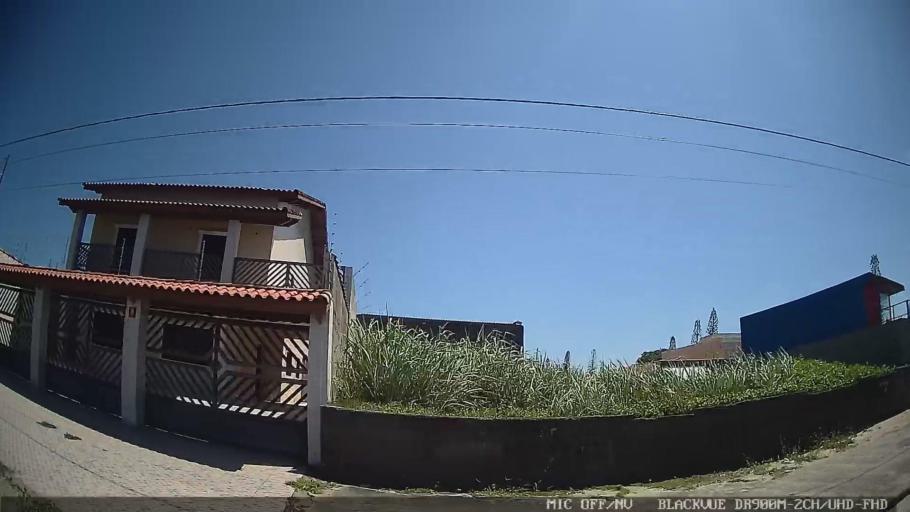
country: BR
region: Sao Paulo
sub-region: Peruibe
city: Peruibe
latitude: -24.3121
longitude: -46.9783
